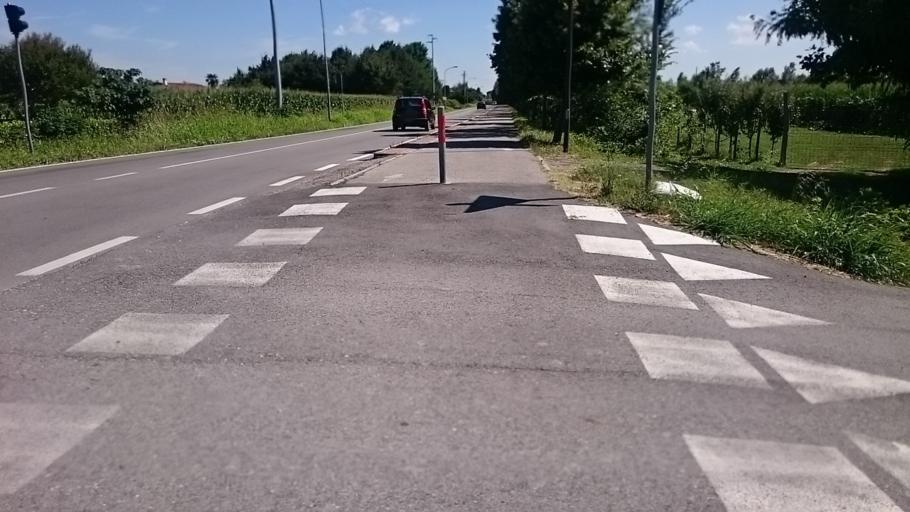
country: IT
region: Veneto
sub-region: Provincia di Venezia
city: Arino
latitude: 45.4334
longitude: 12.0516
